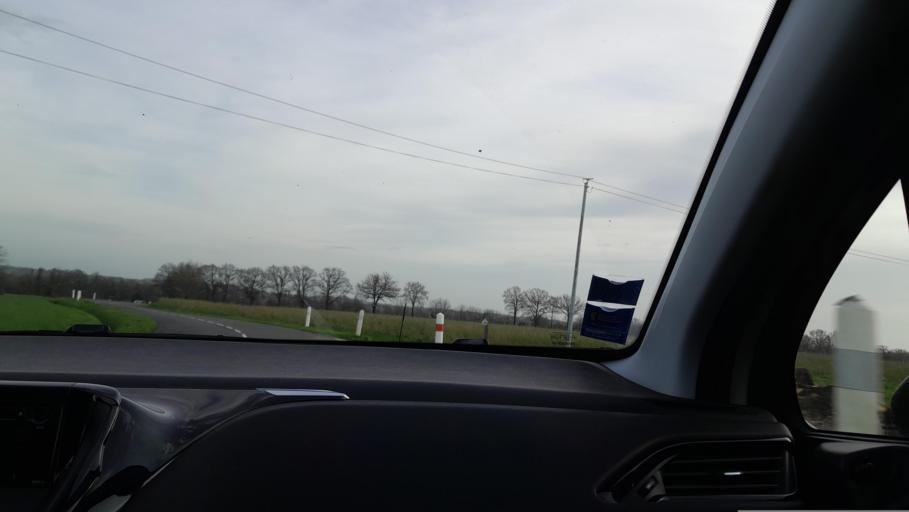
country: FR
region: Brittany
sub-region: Departement d'Ille-et-Vilaine
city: La Guerche-de-Bretagne
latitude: 47.9575
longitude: -1.1640
